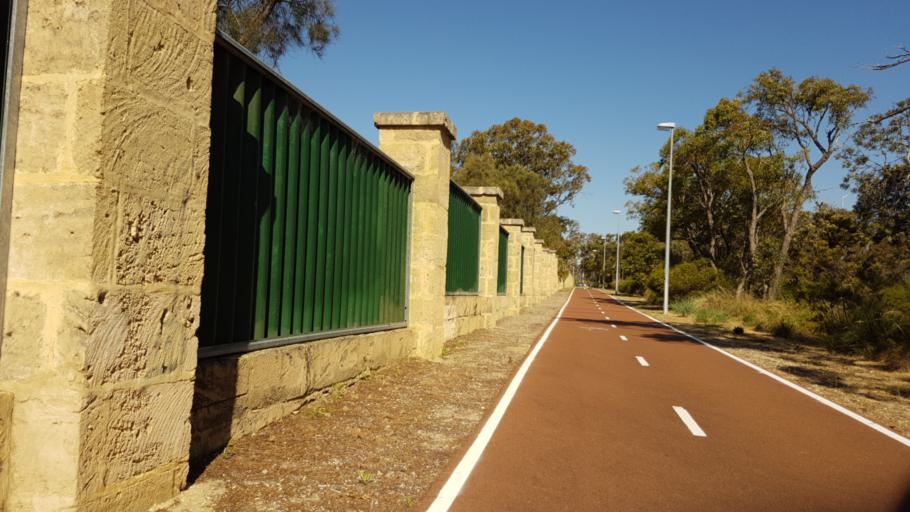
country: AU
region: Western Australia
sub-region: Stirling
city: Balcatta
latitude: -31.8562
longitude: 115.8102
